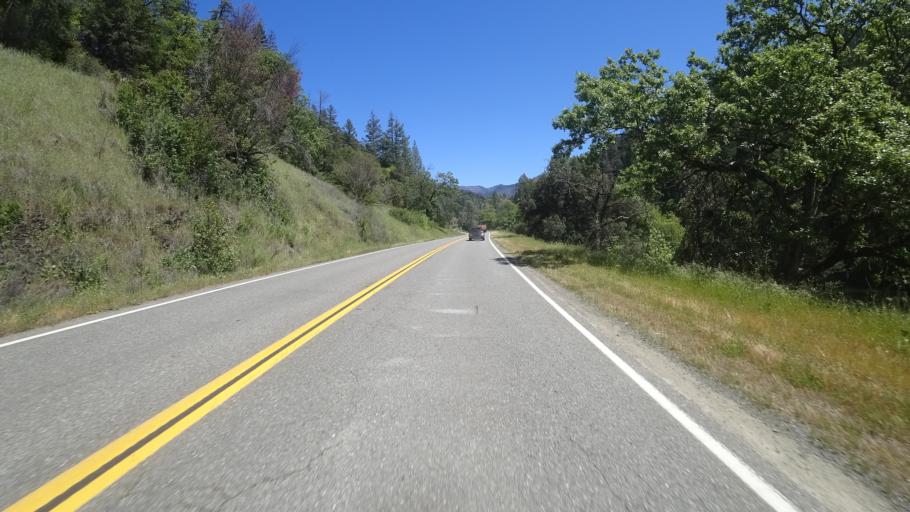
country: US
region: California
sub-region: Trinity County
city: Hayfork
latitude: 40.7394
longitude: -123.2467
